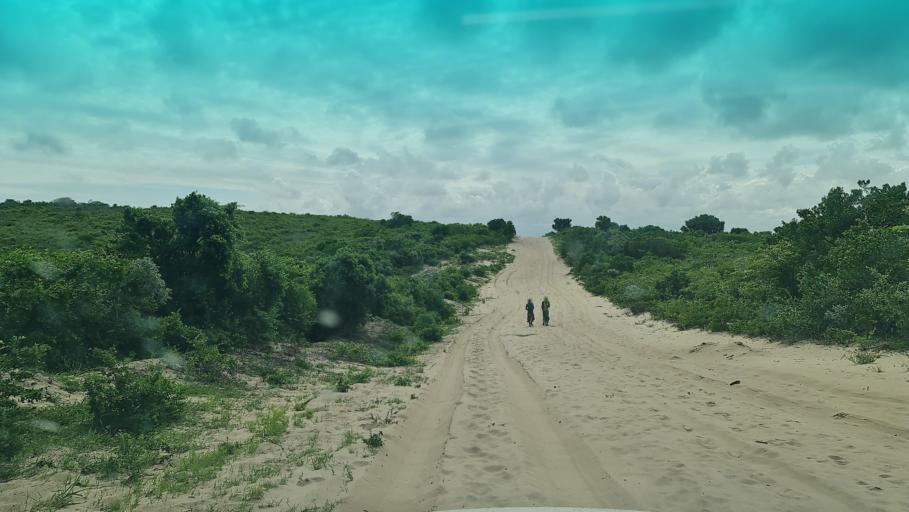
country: MZ
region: Maputo
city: Manhica
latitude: -25.4415
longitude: 32.9417
